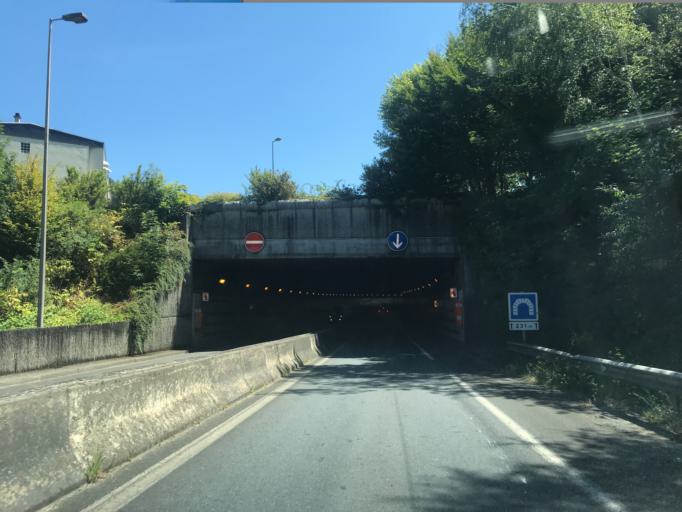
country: FR
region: Limousin
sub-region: Departement de la Correze
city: Tulle
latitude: 45.2510
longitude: 1.7623
